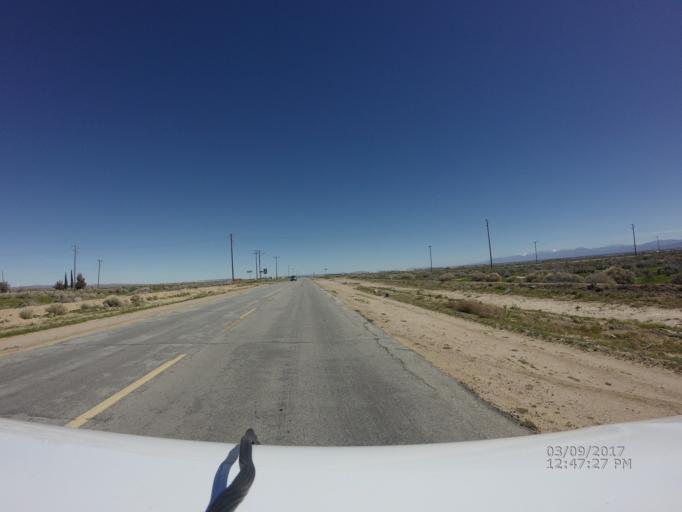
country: US
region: California
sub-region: Los Angeles County
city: Quartz Hill
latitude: 34.7475
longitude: -118.2556
